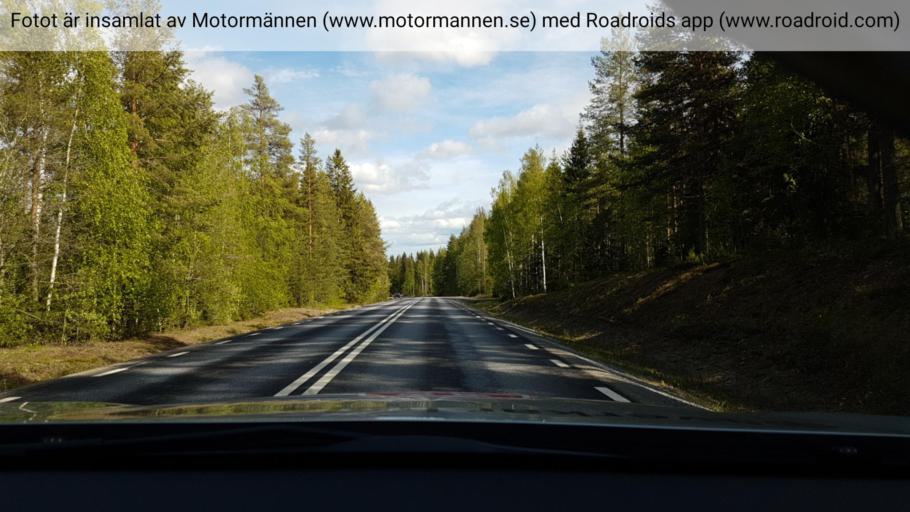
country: SE
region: Vaesterbotten
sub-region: Bjurholms Kommun
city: Bjurholm
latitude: 63.9225
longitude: 19.1105
